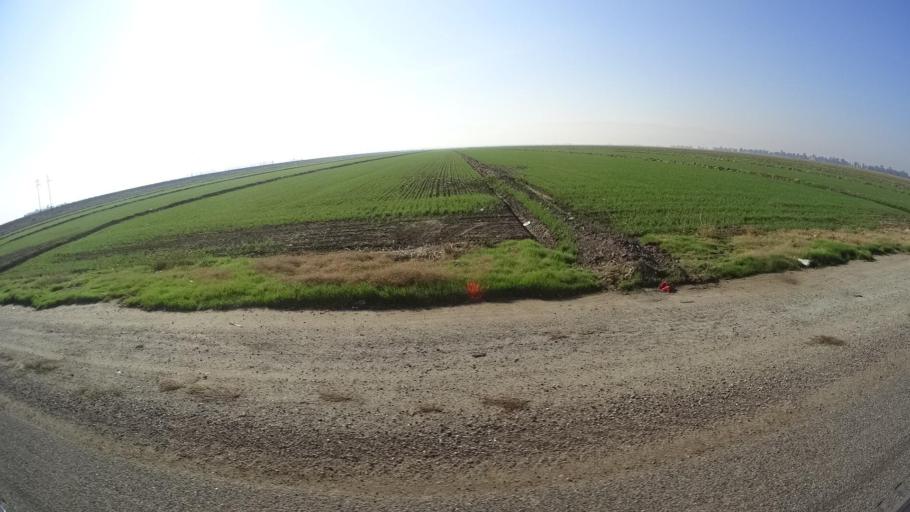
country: US
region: California
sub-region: Kern County
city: Greenfield
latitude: 35.2086
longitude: -118.9787
